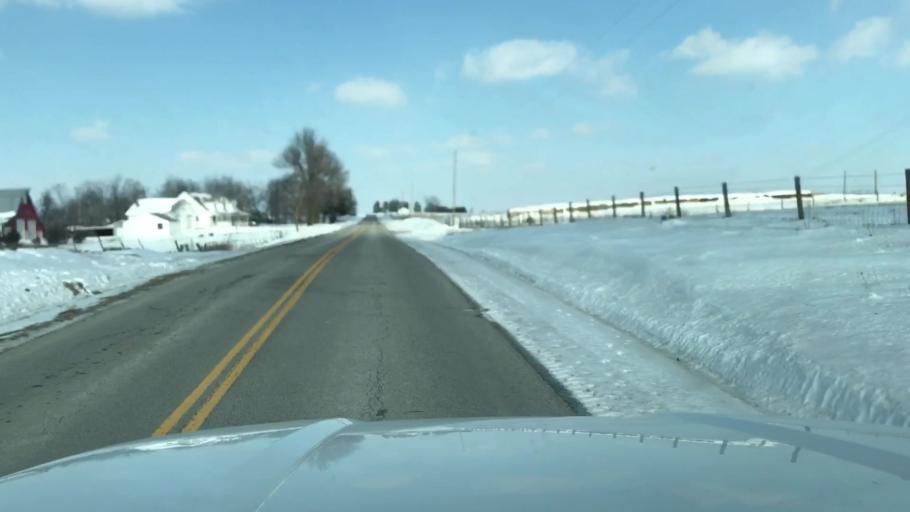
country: US
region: Missouri
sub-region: Nodaway County
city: Maryville
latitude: 40.3668
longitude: -94.7217
